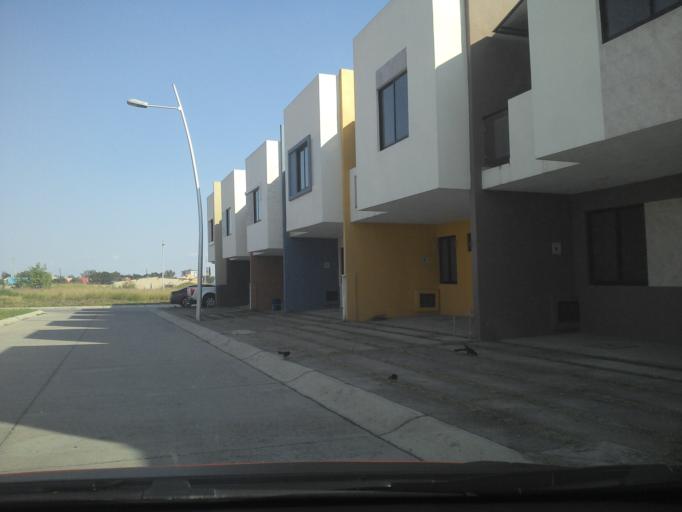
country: MX
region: Jalisco
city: Guadalajara
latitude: 20.6519
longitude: -103.4378
